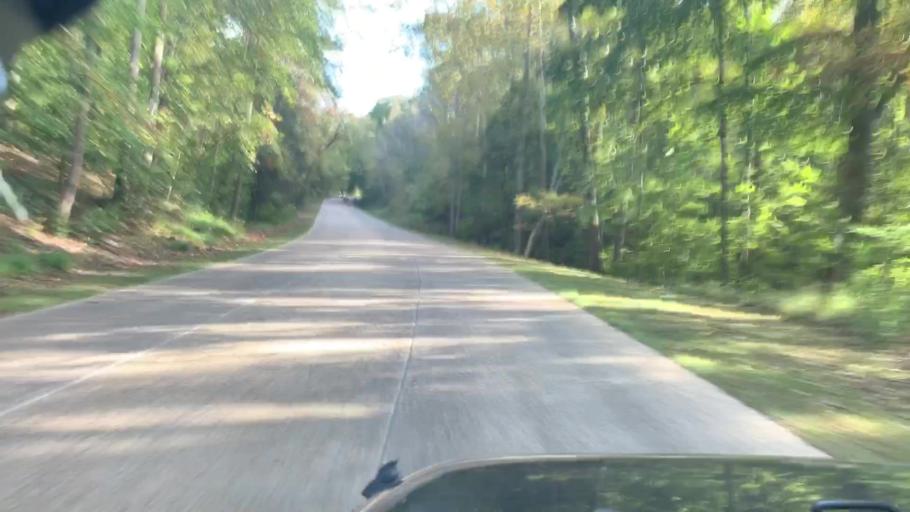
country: US
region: Virginia
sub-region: City of Williamsburg
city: Williamsburg
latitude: 37.2535
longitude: -76.7033
